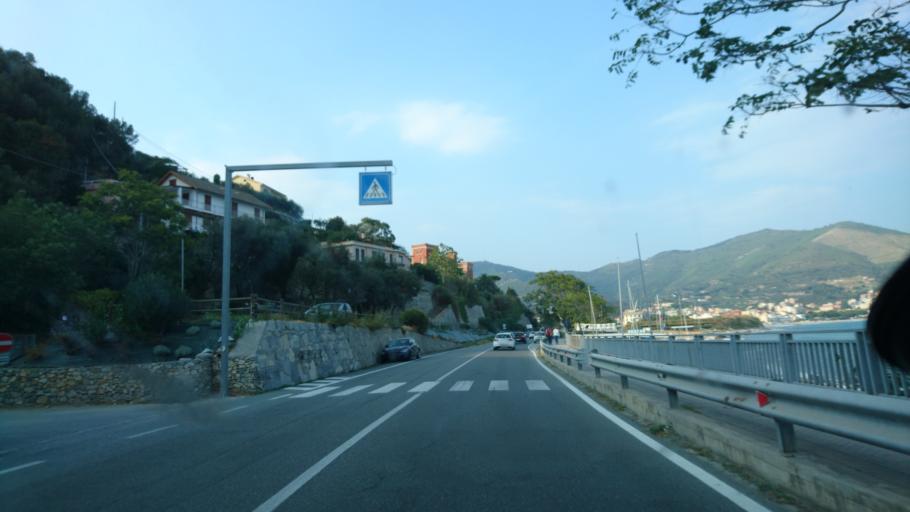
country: IT
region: Liguria
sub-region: Provincia di Savona
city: Noli
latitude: 44.2159
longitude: 8.4155
